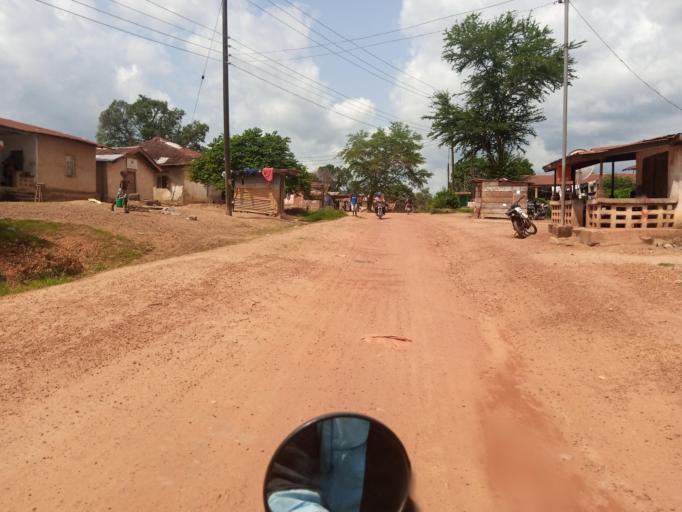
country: SL
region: Southern Province
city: Bo
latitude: 7.9757
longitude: -11.7348
